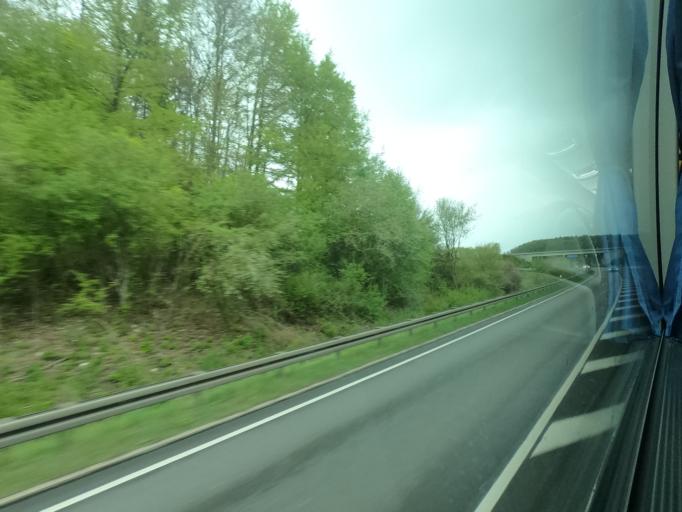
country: DE
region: Baden-Wuerttemberg
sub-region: Regierungsbezirk Stuttgart
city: Nattheim
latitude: 48.6900
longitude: 10.2108
